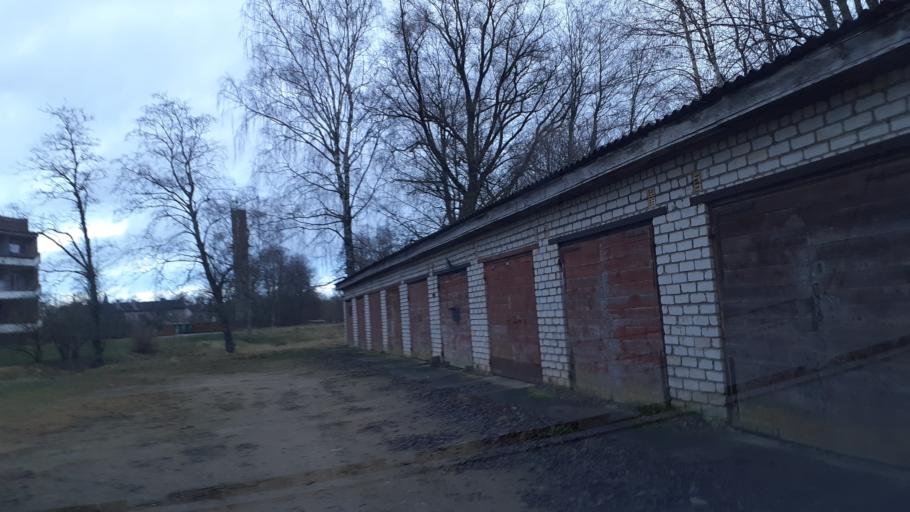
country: LV
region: Talsu Rajons
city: Stende
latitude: 57.0655
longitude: 22.2863
